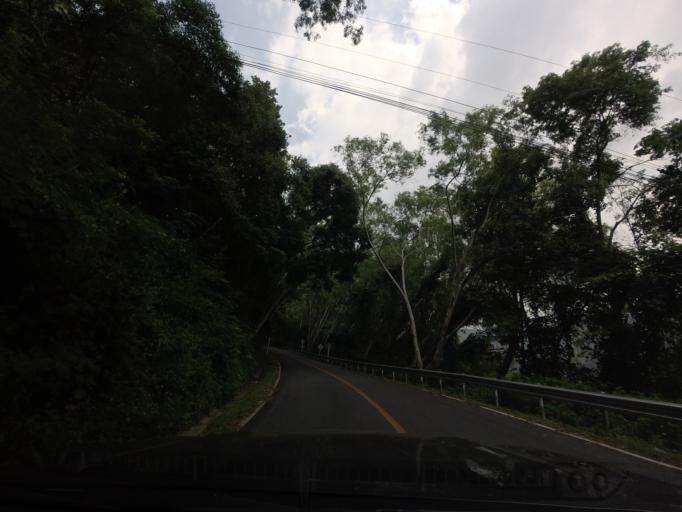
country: TH
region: Nan
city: Pua
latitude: 19.1826
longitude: 100.9940
